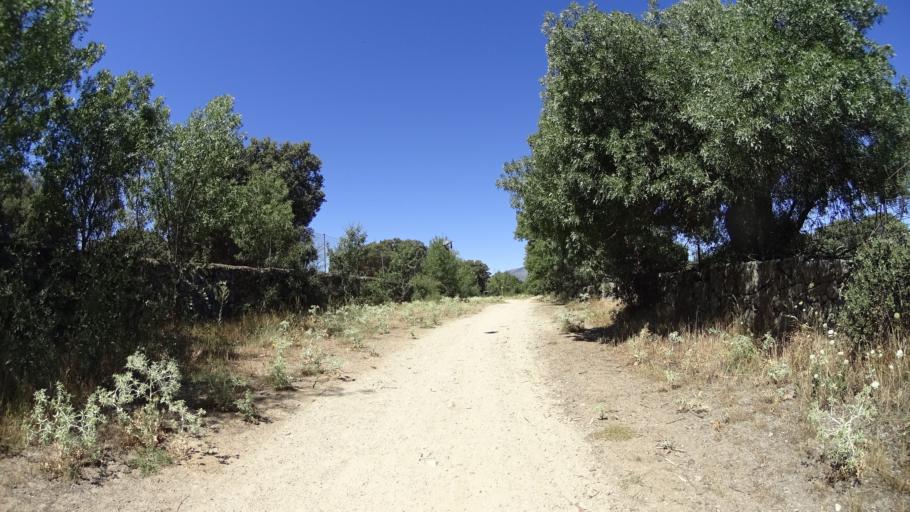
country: ES
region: Madrid
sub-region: Provincia de Madrid
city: Alpedrete
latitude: 40.6474
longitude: -4.0151
